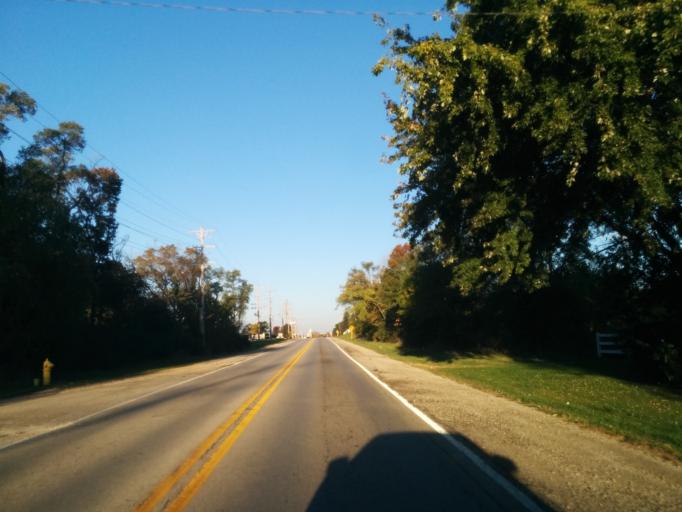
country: US
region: Illinois
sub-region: DuPage County
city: Glendale Heights
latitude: 41.8968
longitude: -88.0964
